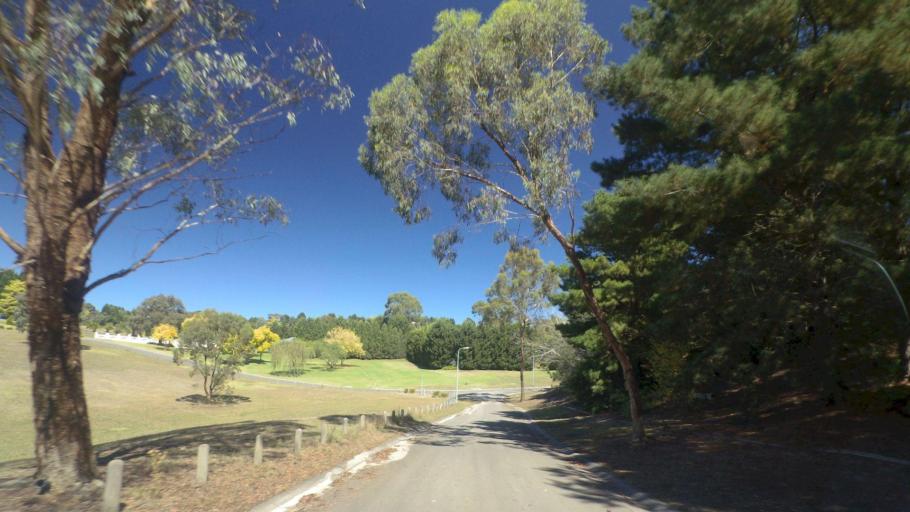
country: AU
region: Victoria
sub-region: Manningham
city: Donvale
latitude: -37.7797
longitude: 145.1876
